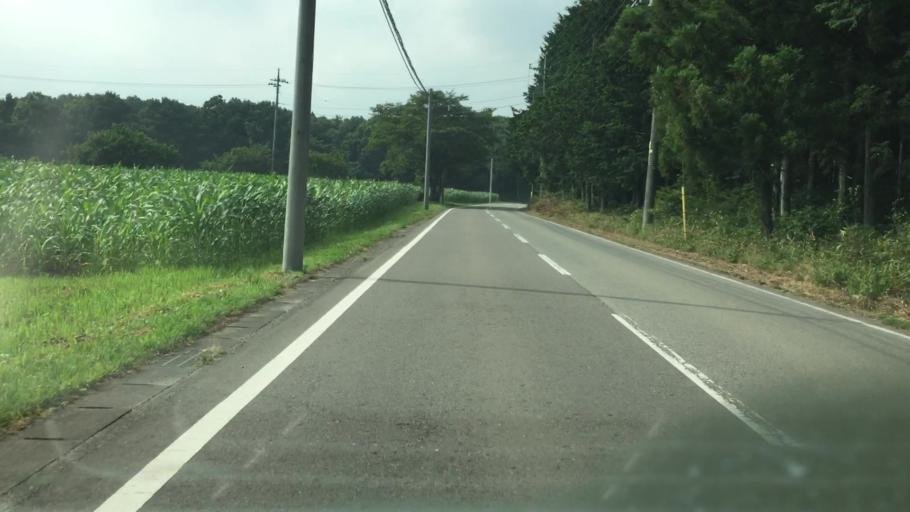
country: JP
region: Tochigi
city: Kuroiso
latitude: 36.9530
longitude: 139.9595
